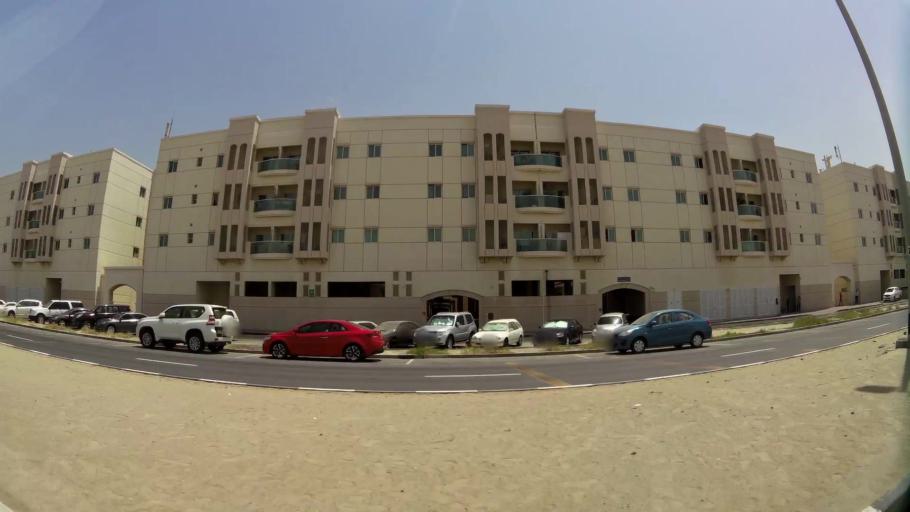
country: AE
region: Ash Shariqah
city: Sharjah
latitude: 25.2760
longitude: 55.4048
